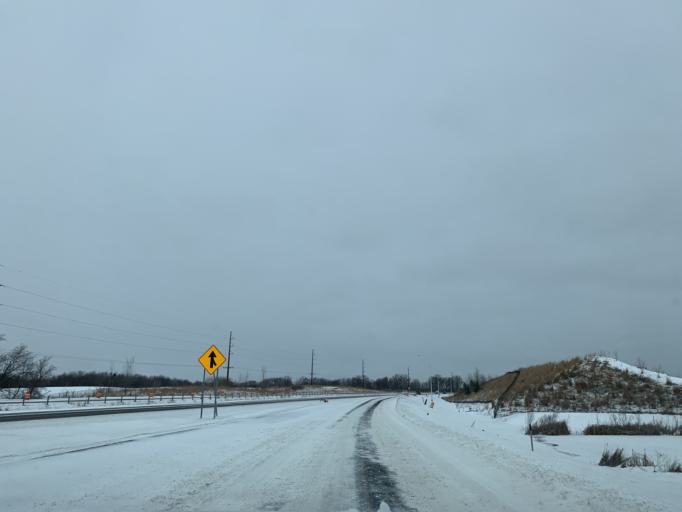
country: US
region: Minnesota
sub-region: Carver County
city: Chaska
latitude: 44.7932
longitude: -93.6314
